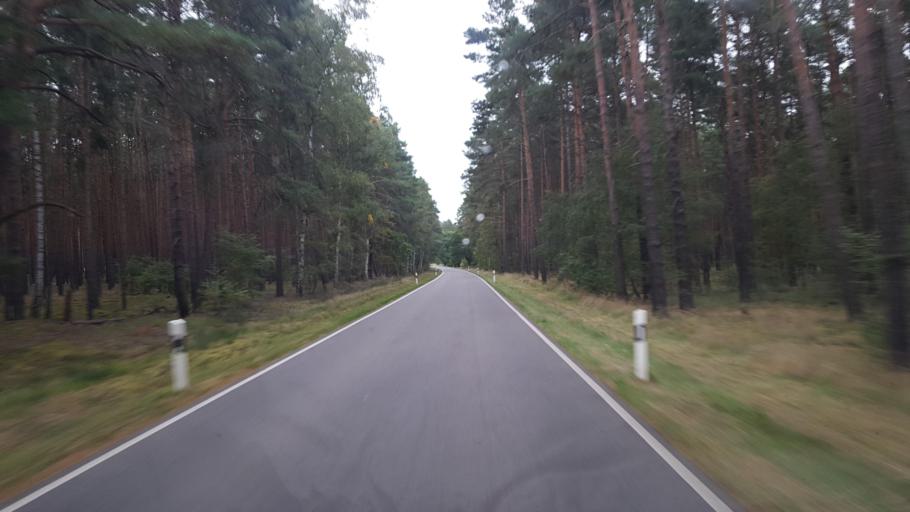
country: DE
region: Brandenburg
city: Luckau
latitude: 51.8833
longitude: 13.6721
